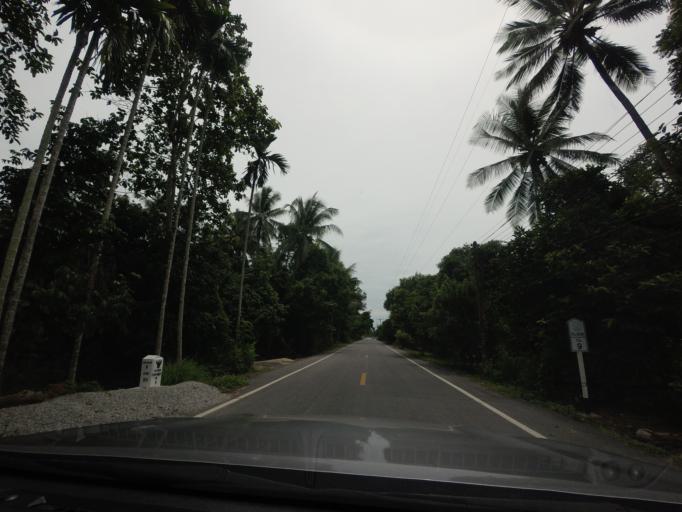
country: TH
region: Pattani
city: Kapho
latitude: 6.6126
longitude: 101.5404
